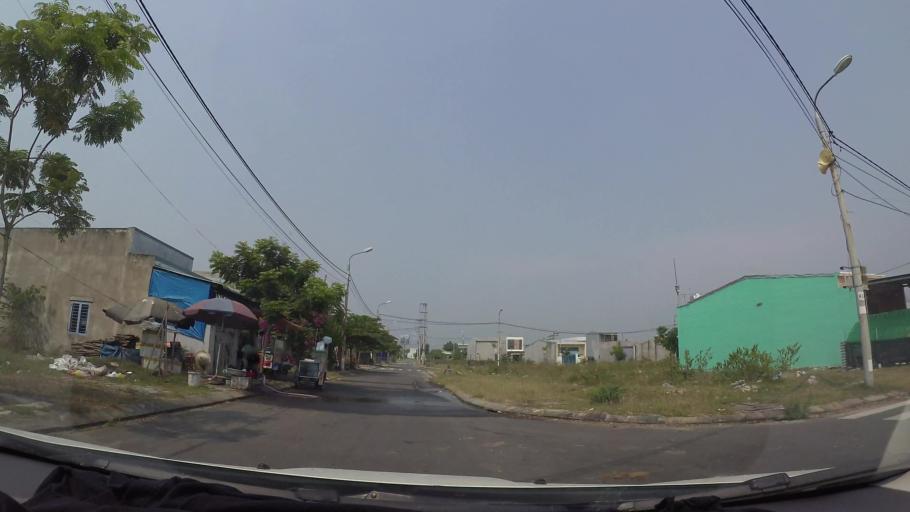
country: VN
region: Da Nang
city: Cam Le
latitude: 15.9702
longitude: 108.2131
